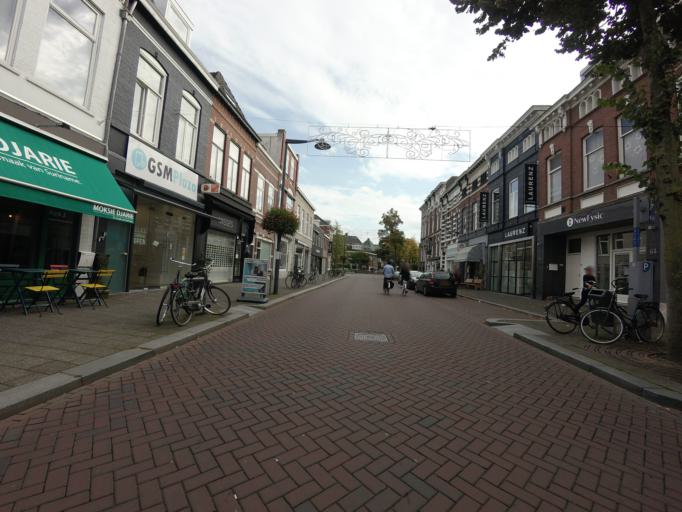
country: NL
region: North Brabant
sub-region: Gemeente Breda
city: Breda
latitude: 51.5770
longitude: 4.7811
